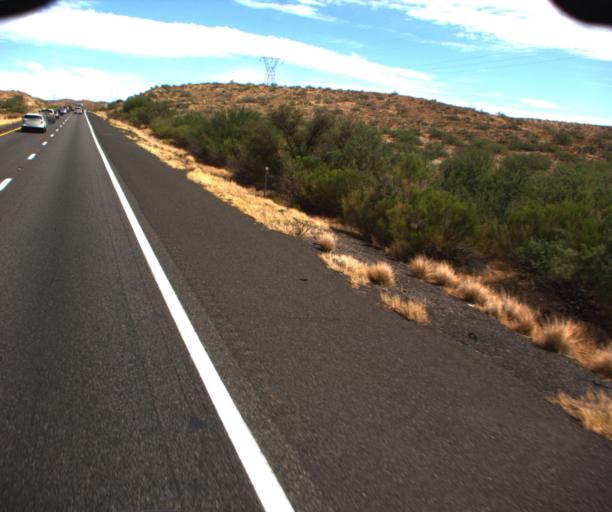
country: US
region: Arizona
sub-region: Yavapai County
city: Cordes Lakes
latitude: 34.2452
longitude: -112.1120
